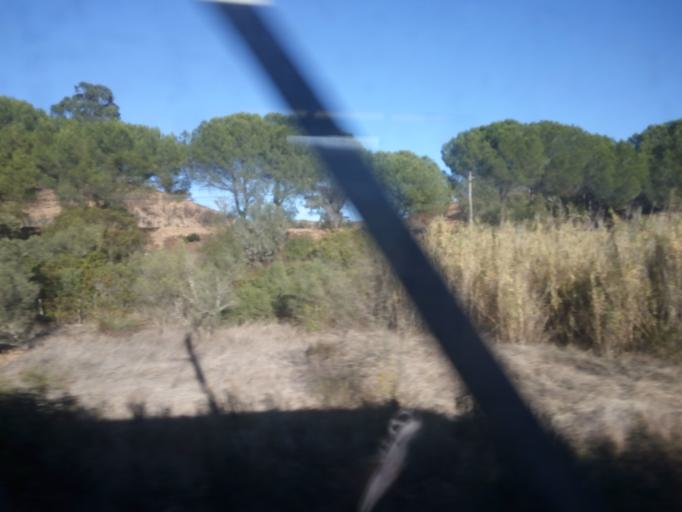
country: PT
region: Faro
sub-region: Silves
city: Sao Bartolomeu de Messines
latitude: 37.3190
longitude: -8.3282
